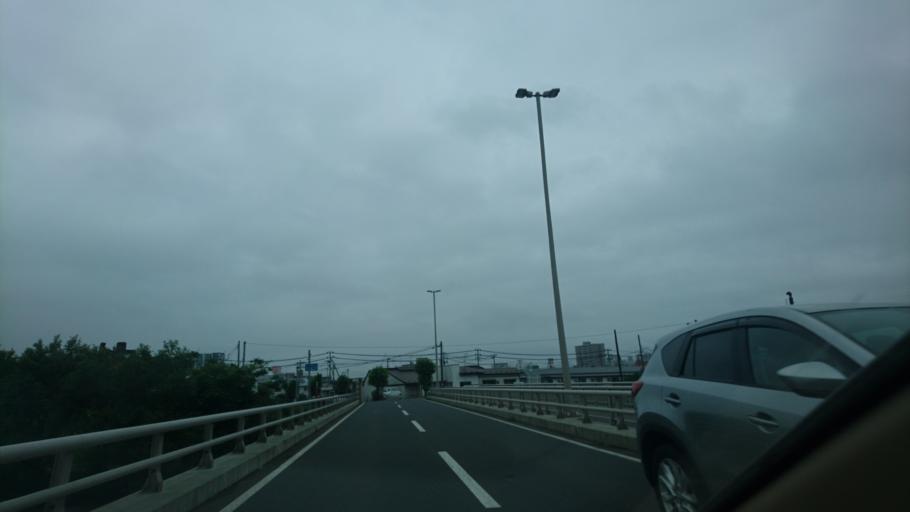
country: JP
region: Iwate
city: Kitakami
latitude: 39.2778
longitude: 141.1135
